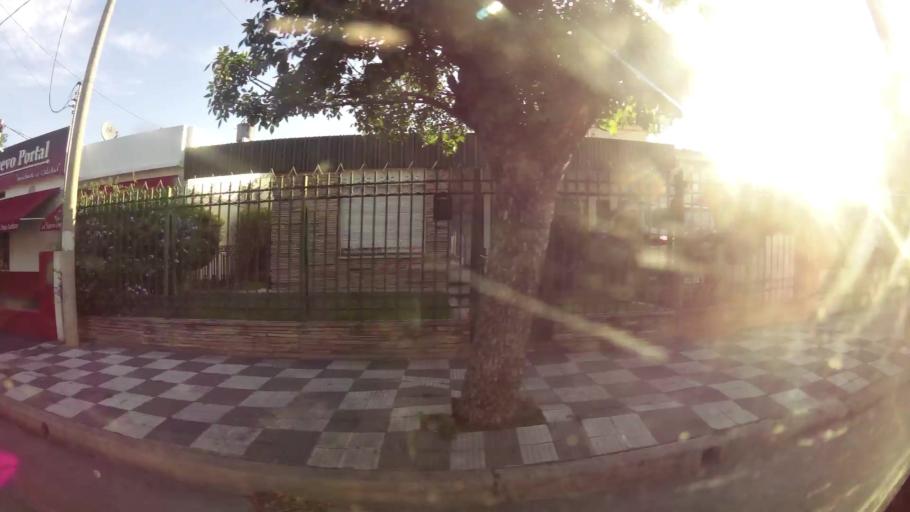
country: AR
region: Cordoba
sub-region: Departamento de Capital
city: Cordoba
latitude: -31.3890
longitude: -64.2204
